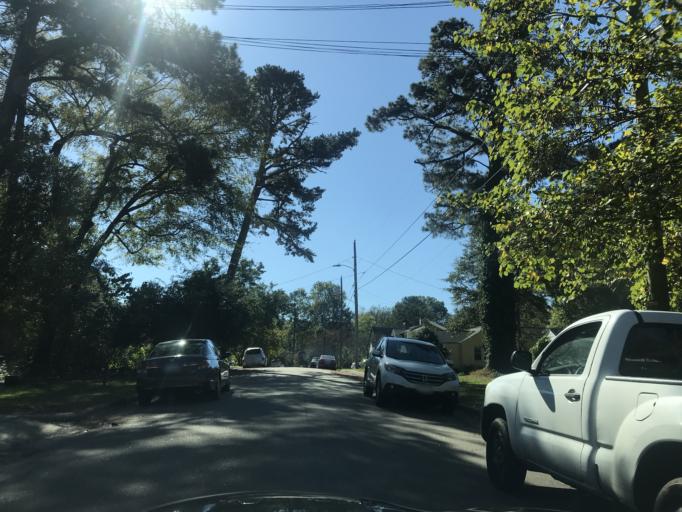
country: US
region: North Carolina
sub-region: Wake County
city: Raleigh
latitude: 35.7950
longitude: -78.6269
